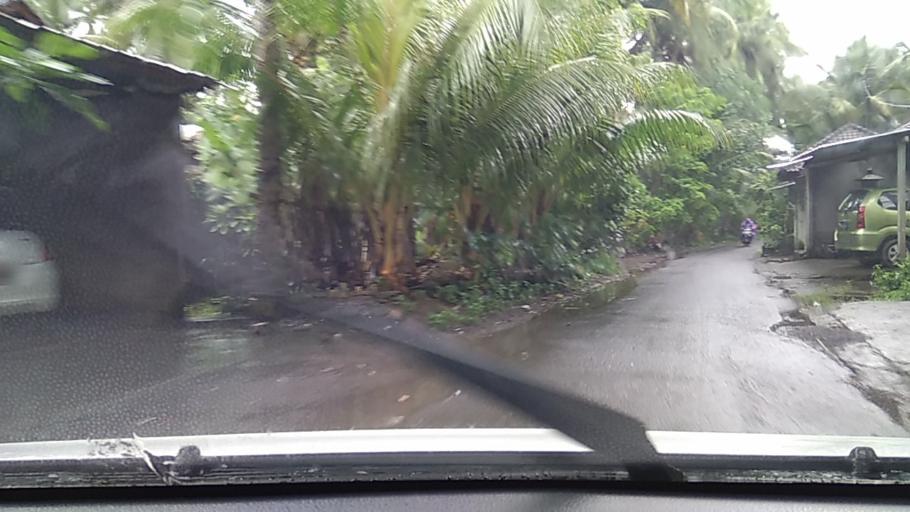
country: ID
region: Bali
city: Banjar Bugbug
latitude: -8.5099
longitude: 115.5786
